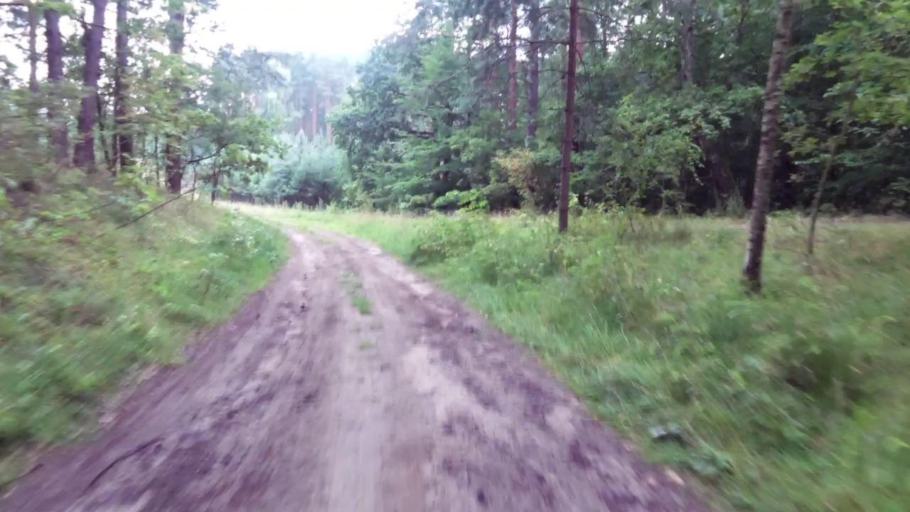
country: PL
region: West Pomeranian Voivodeship
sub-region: Powiat szczecinecki
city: Lubowo
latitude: 53.5985
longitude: 16.3846
